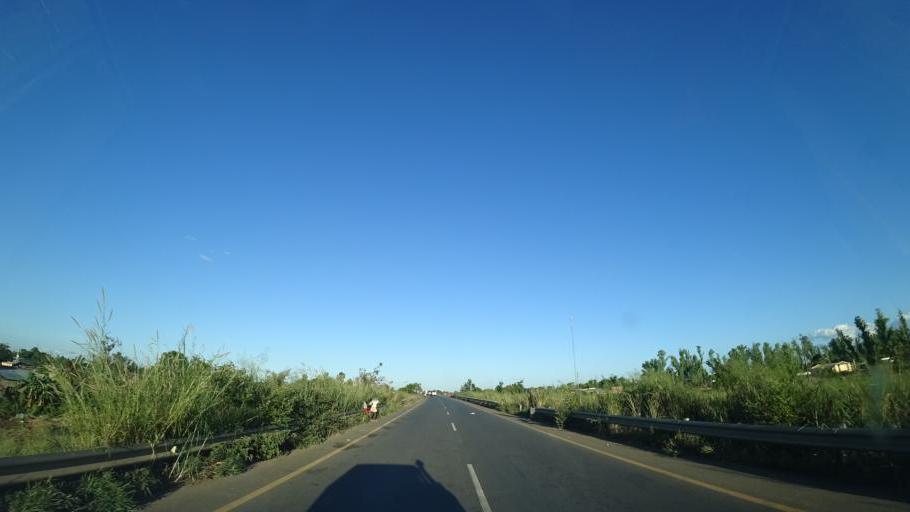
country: MZ
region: Sofala
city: Dondo
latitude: -19.3303
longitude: 34.3135
